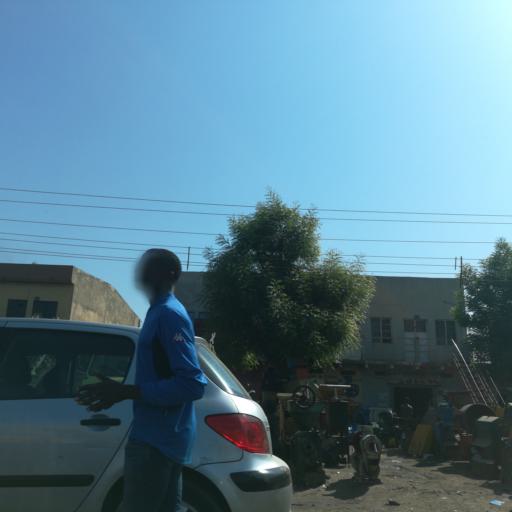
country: NG
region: Kano
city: Kano
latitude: 12.0131
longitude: 8.5326
